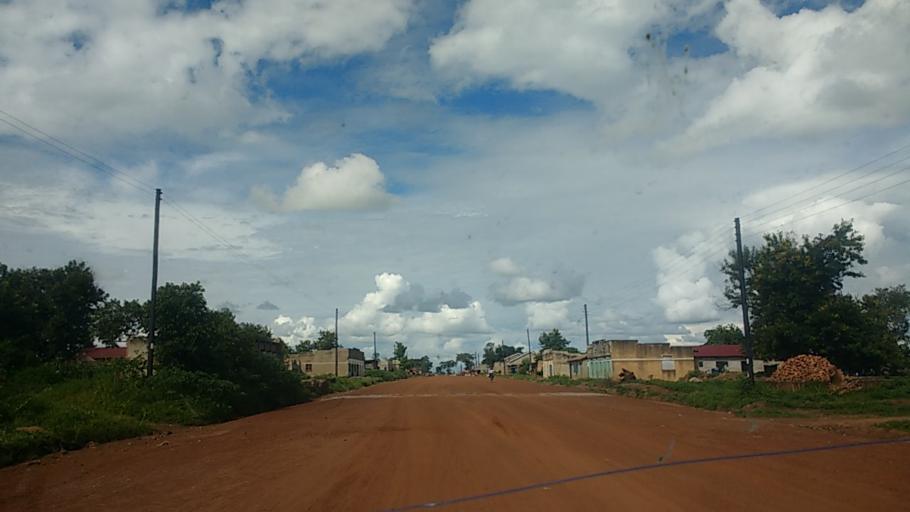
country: UG
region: Eastern Region
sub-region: Katakwi District
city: Katakwi
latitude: 1.9195
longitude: 33.9842
